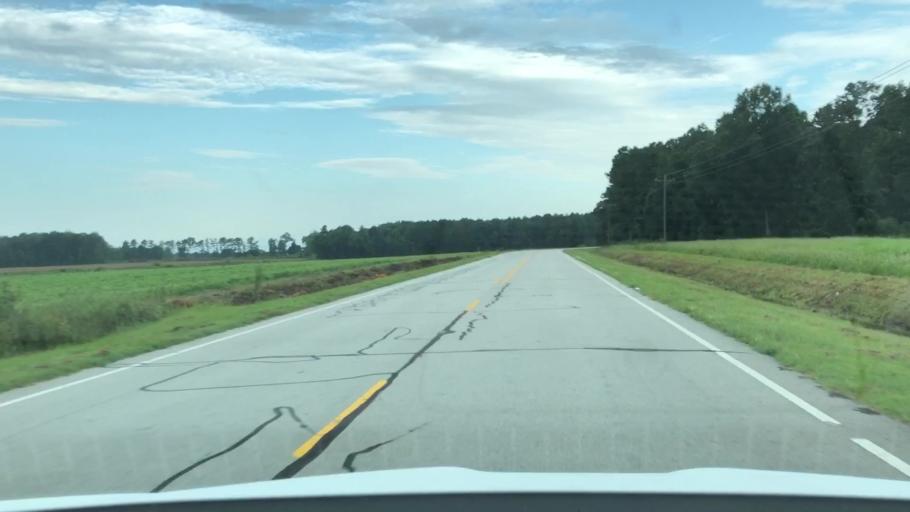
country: US
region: North Carolina
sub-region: Jones County
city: Trenton
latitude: 35.1082
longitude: -77.5032
